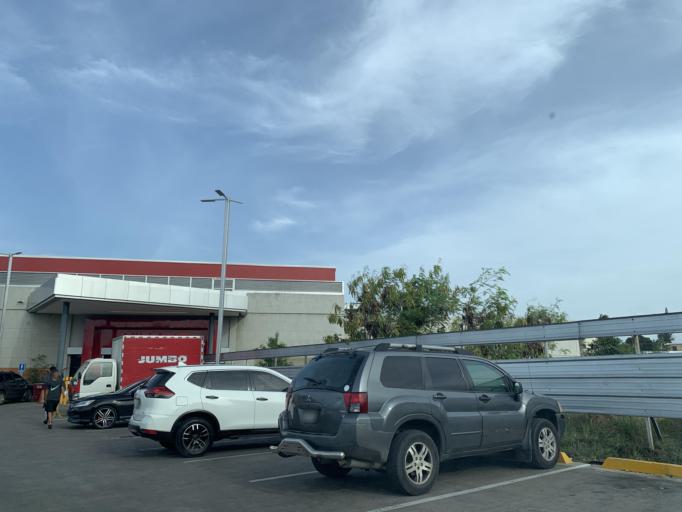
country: DO
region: Puerto Plata
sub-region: Puerto Plata
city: Puerto Plata
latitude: 19.7818
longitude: -70.6738
